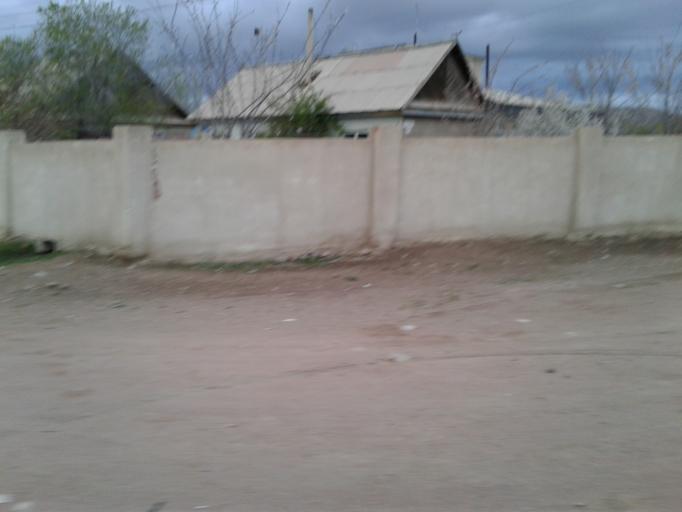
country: KG
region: Ysyk-Koel
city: Bokombayevskoye
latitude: 42.1165
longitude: 76.9877
